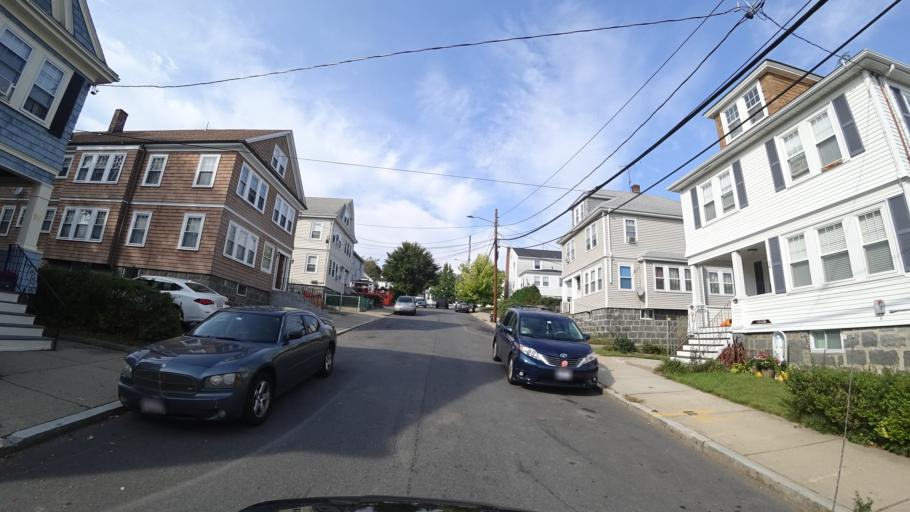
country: US
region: Massachusetts
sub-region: Norfolk County
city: Milton
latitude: 42.2775
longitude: -71.0726
